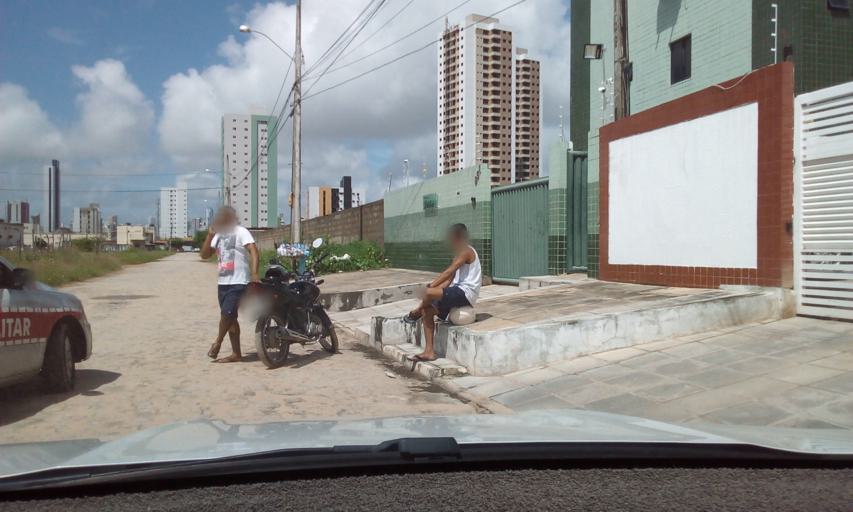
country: BR
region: Paraiba
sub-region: Joao Pessoa
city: Joao Pessoa
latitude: -7.0813
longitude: -34.8422
